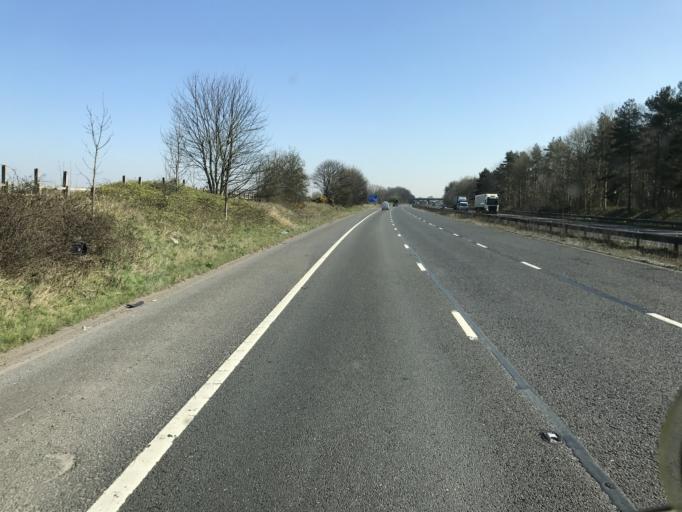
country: GB
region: England
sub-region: Borough of Halton
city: Daresbury
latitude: 53.3322
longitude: -2.6073
